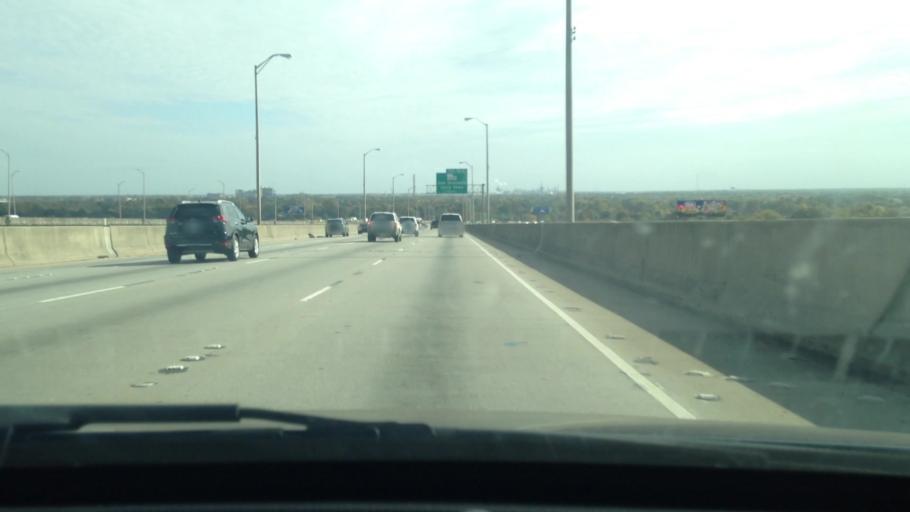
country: US
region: Louisiana
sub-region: Jefferson Parish
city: Gretna
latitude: 29.9375
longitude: -90.0482
